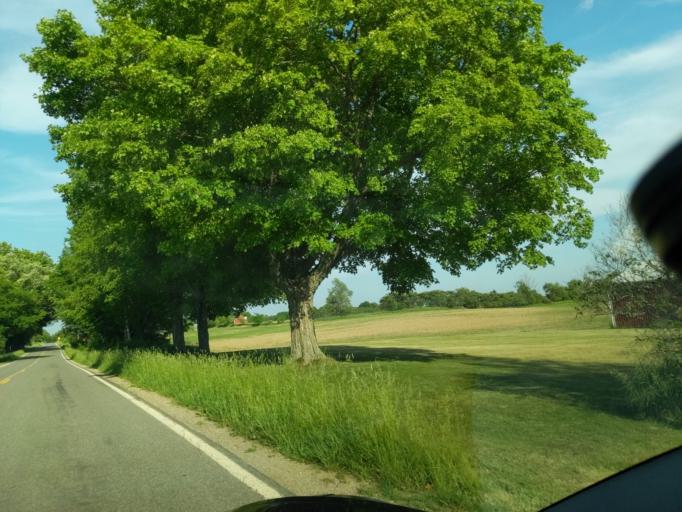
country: US
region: Michigan
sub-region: Barry County
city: Nashville
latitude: 42.6251
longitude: -85.1016
